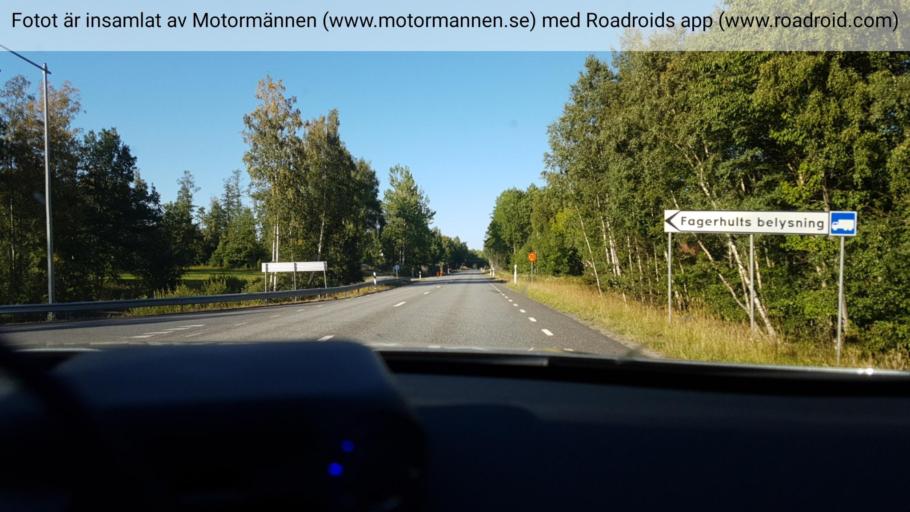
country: SE
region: Joenkoeping
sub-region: Habo Kommun
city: Habo
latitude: 58.0013
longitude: 14.1224
